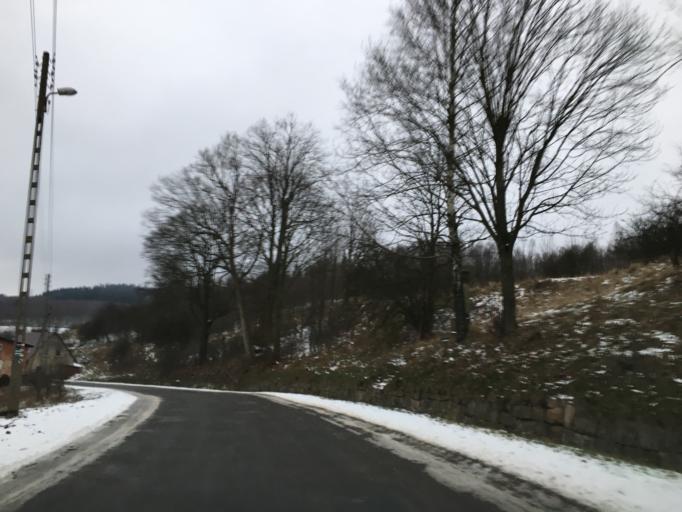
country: CZ
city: Radvanice
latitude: 50.6298
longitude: 16.0416
